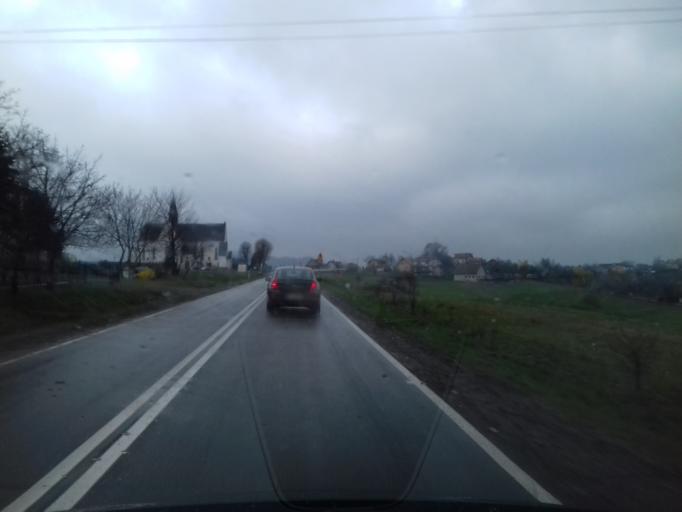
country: PL
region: Lesser Poland Voivodeship
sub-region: Powiat nowosadecki
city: Chelmiec
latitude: 49.6362
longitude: 20.6209
